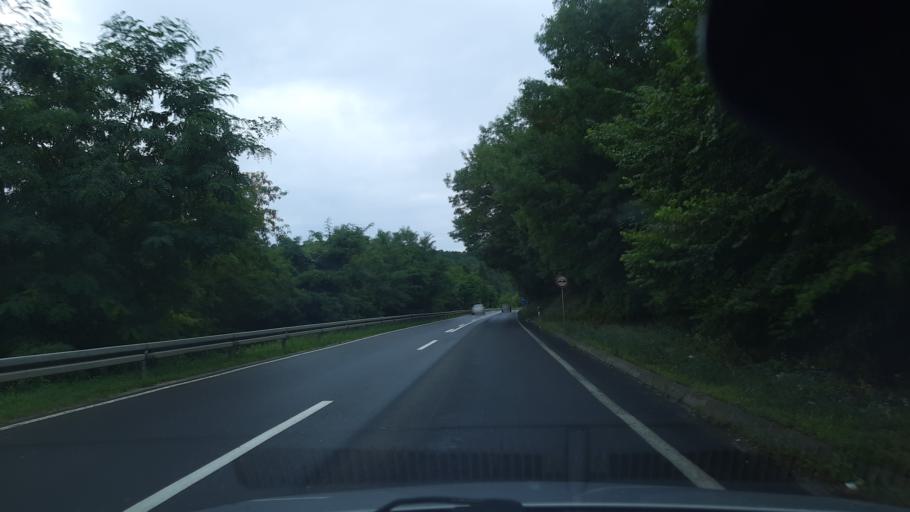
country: RS
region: Central Serbia
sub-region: Sumadijski Okrug
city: Knic
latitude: 43.9652
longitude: 20.8101
